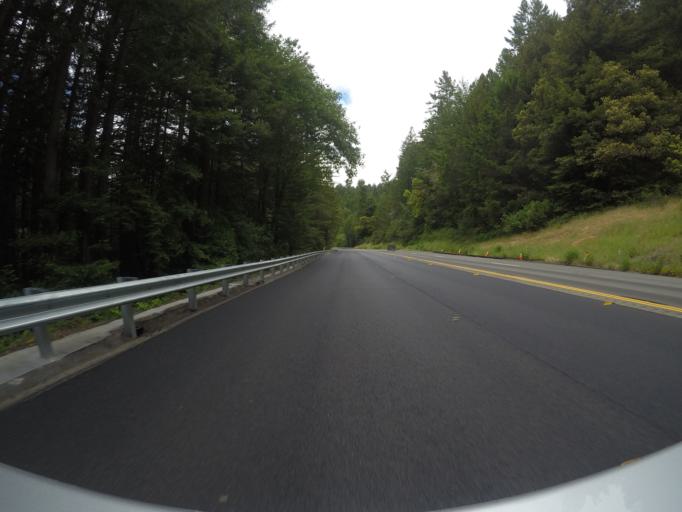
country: US
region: California
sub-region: Humboldt County
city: Redway
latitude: 40.3107
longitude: -123.9074
